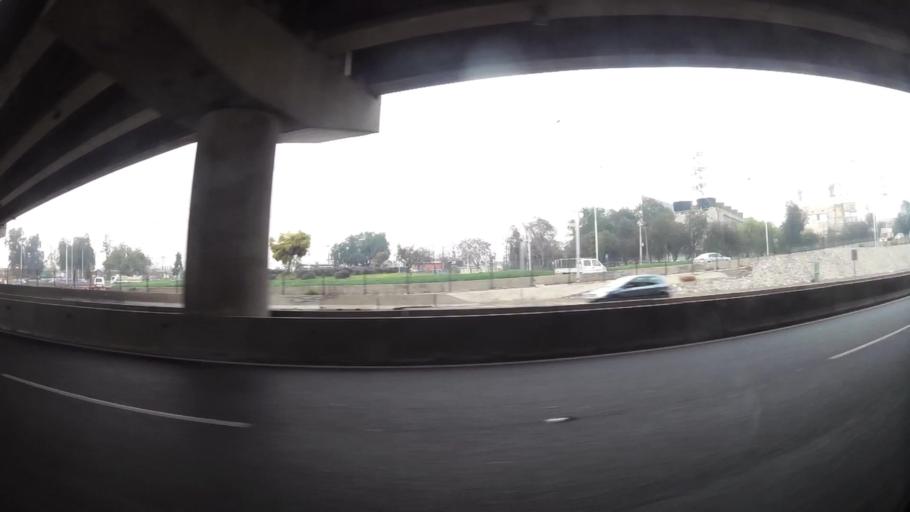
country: CL
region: Santiago Metropolitan
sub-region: Provincia de Santiago
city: Lo Prado
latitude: -33.4165
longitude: -70.6916
